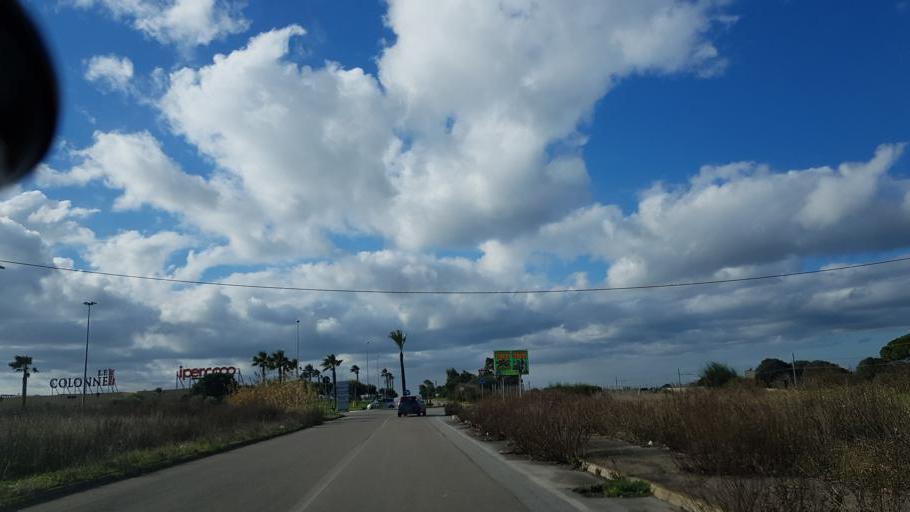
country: IT
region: Apulia
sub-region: Provincia di Brindisi
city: Brindisi
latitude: 40.6216
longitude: 17.9043
